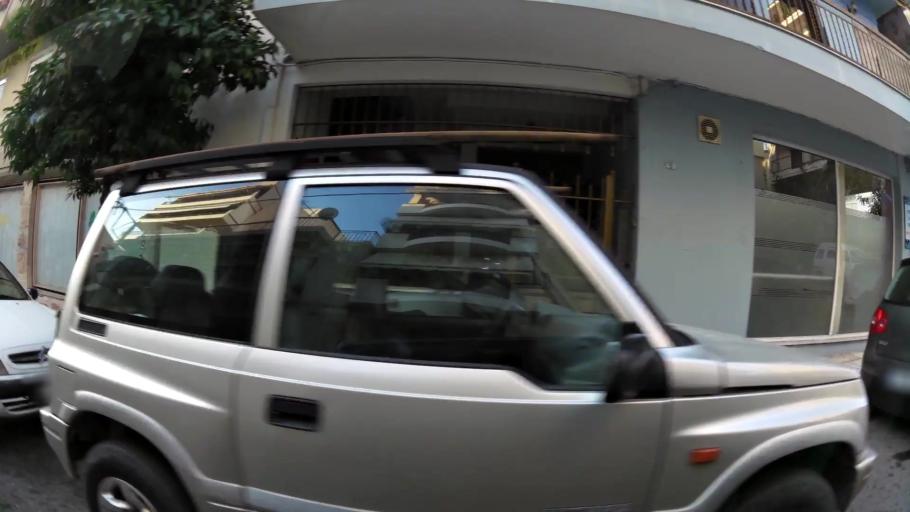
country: GR
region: Attica
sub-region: Nomarchia Athinas
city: Galatsi
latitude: 38.0246
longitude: 23.7497
